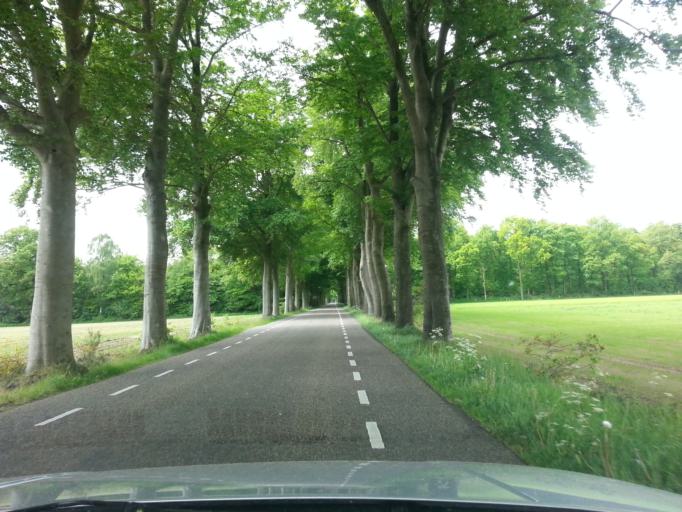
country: NL
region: Gelderland
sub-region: Berkelland
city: Borculo
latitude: 52.0975
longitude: 6.5725
